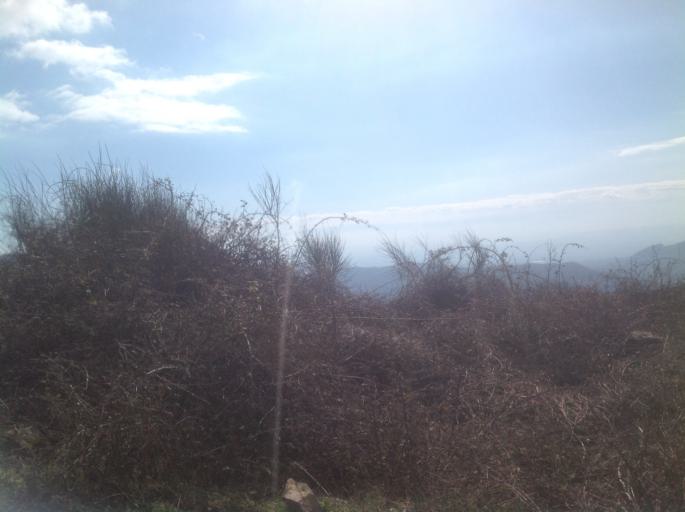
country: IT
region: Calabria
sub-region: Provincia di Cosenza
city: Civita
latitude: 39.8476
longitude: 16.3059
